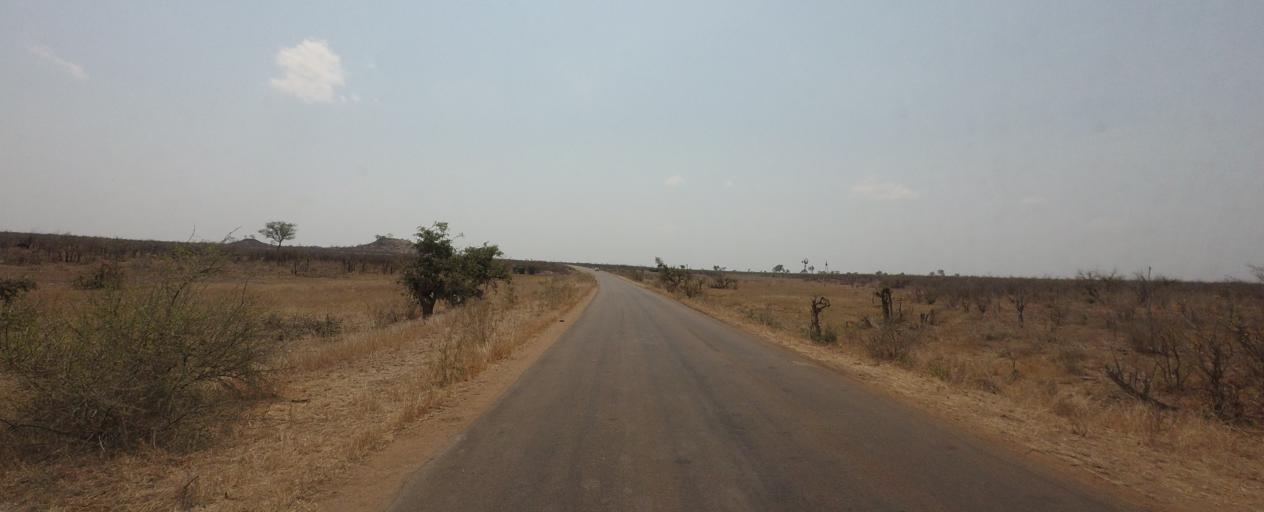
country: ZA
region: Limpopo
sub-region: Mopani District Municipality
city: Phalaborwa
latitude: -23.5003
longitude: 31.4021
